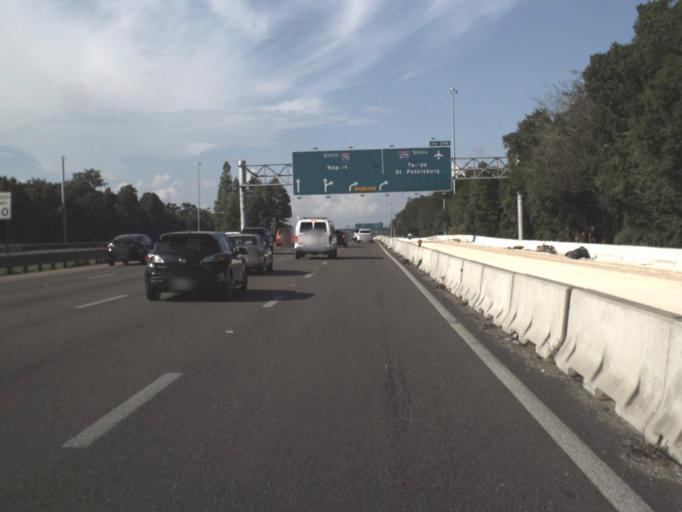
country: US
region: Florida
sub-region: Hillsborough County
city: Pebble Creek
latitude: 28.1839
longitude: -82.3887
